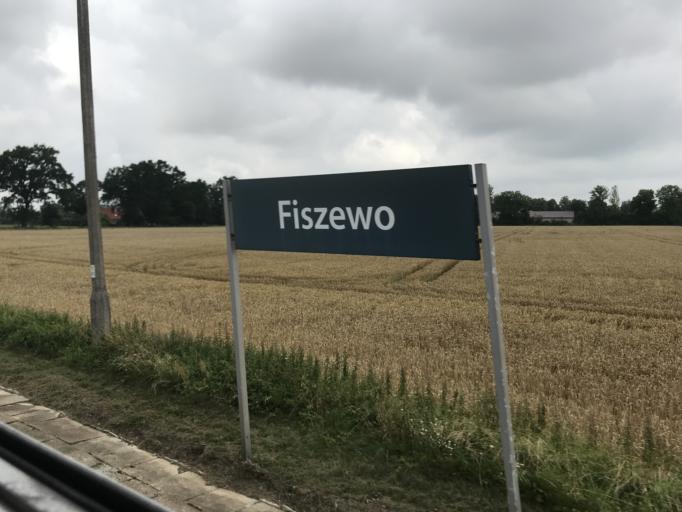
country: PL
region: Pomeranian Voivodeship
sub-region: Powiat malborski
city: Stare Pole
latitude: 54.0678
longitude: 19.2496
